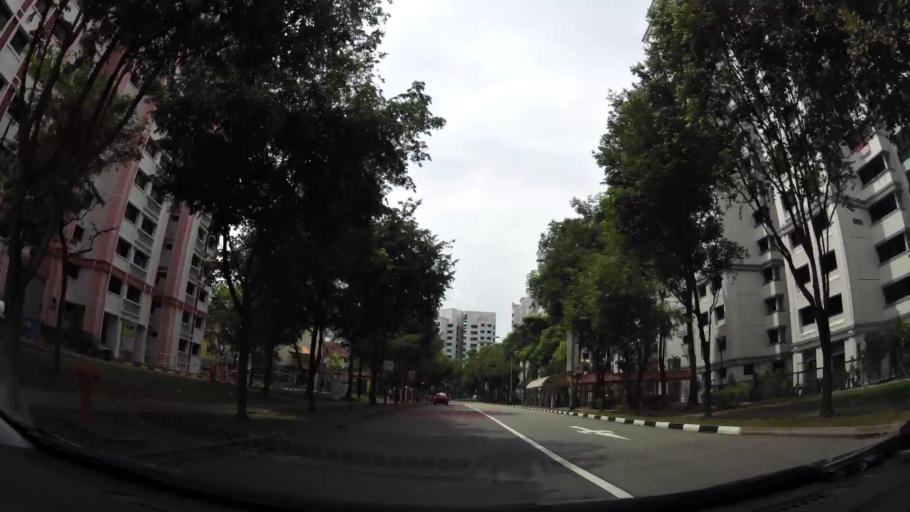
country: MY
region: Johor
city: Johor Bahru
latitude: 1.4033
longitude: 103.7481
